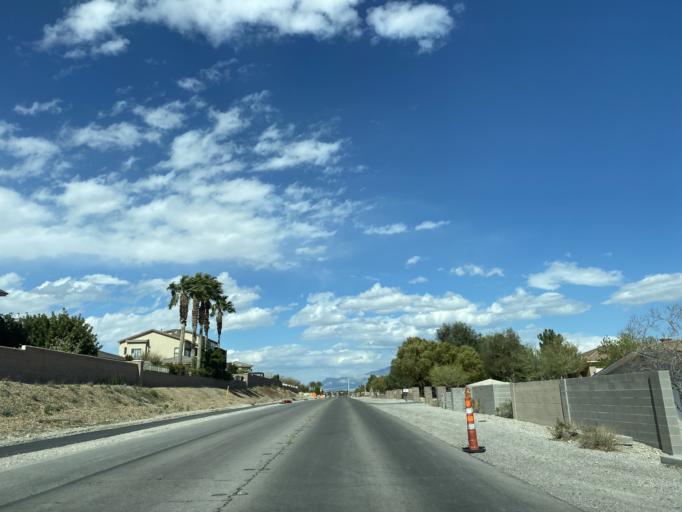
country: US
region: Nevada
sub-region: Clark County
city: Summerlin South
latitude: 36.2443
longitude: -115.3084
